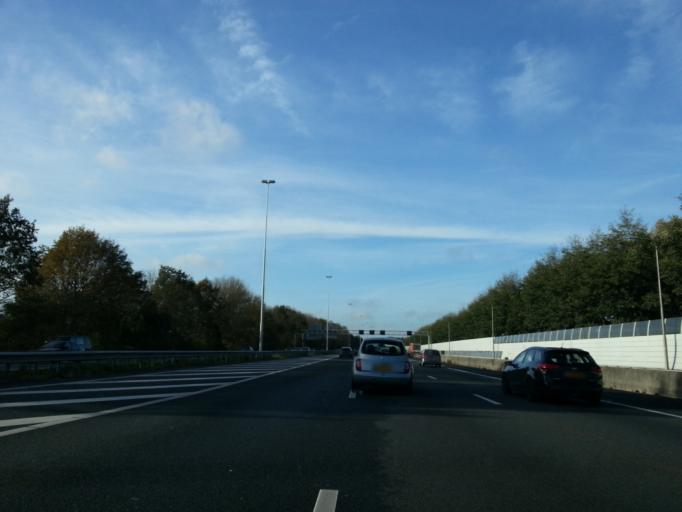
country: NL
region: South Holland
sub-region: Gemeente Rotterdam
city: Rotterdam
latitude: 51.9464
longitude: 4.5076
